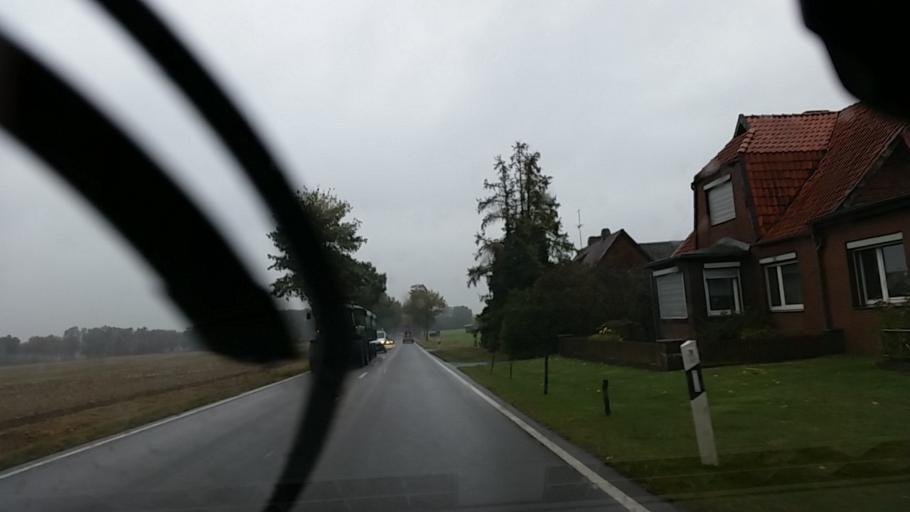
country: DE
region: Lower Saxony
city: Luder
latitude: 52.7879
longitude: 10.7156
